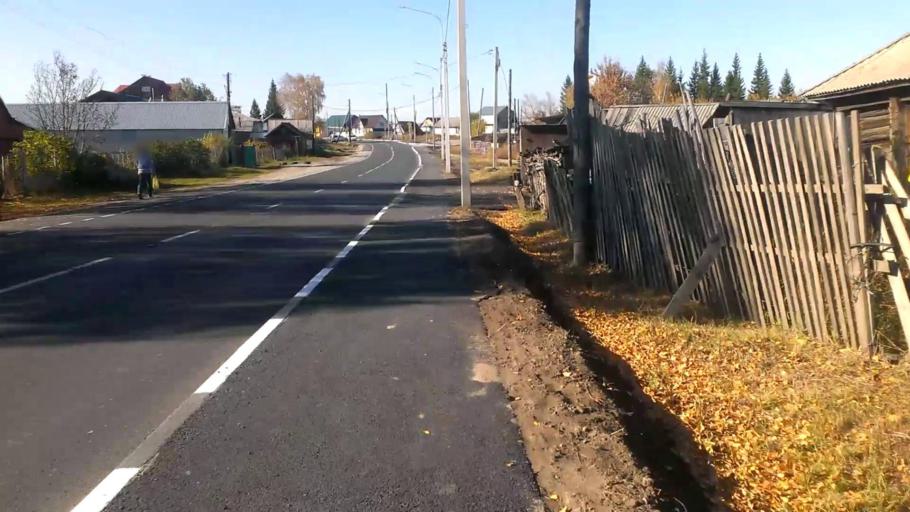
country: RU
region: Altai Krai
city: Sannikovo
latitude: 53.3151
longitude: 83.9600
